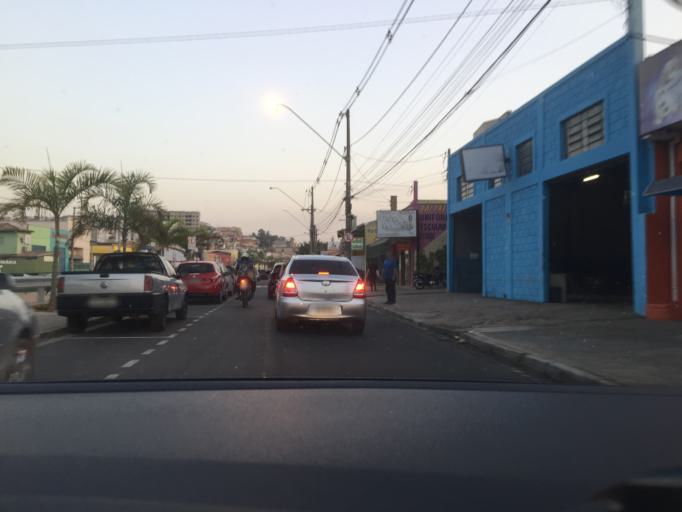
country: BR
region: Sao Paulo
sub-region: Varzea Paulista
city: Varzea Paulista
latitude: -23.2179
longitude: -46.8403
